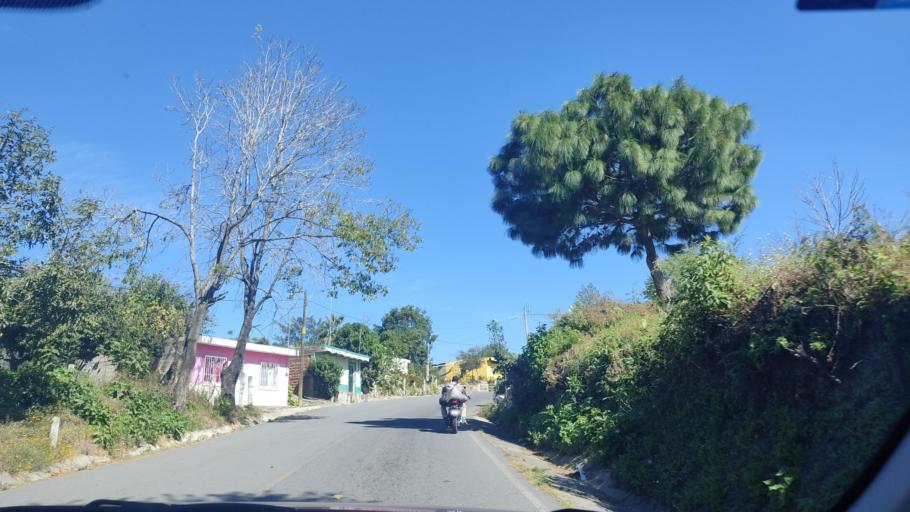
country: MX
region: Nayarit
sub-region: Jala
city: Rosa Blanca
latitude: 21.1074
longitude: -104.3575
